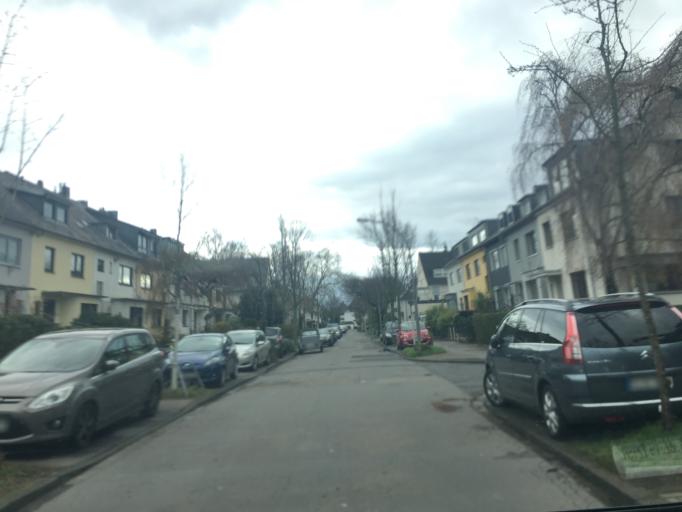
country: DE
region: North Rhine-Westphalia
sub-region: Regierungsbezirk Koln
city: Bilderstoeckchen
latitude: 50.9629
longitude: 6.9202
